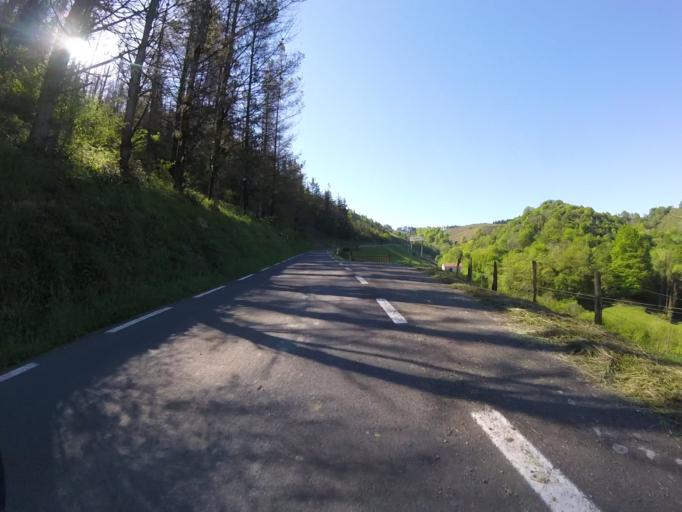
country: ES
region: Basque Country
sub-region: Provincia de Guipuzcoa
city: Aizarnazabal
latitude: 43.2247
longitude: -2.2137
